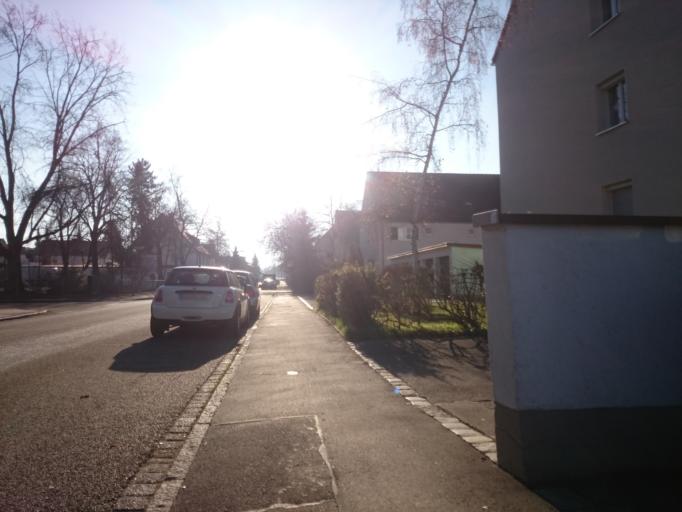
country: DE
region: Bavaria
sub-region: Swabia
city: Konigsbrunn
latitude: 48.3146
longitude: 10.9029
